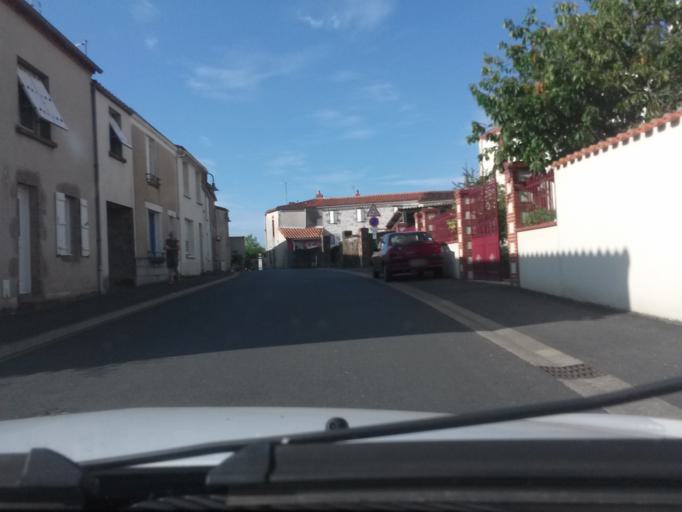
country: FR
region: Pays de la Loire
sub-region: Departement de la Vendee
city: La Bernardiere
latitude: 47.0485
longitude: -1.2667
